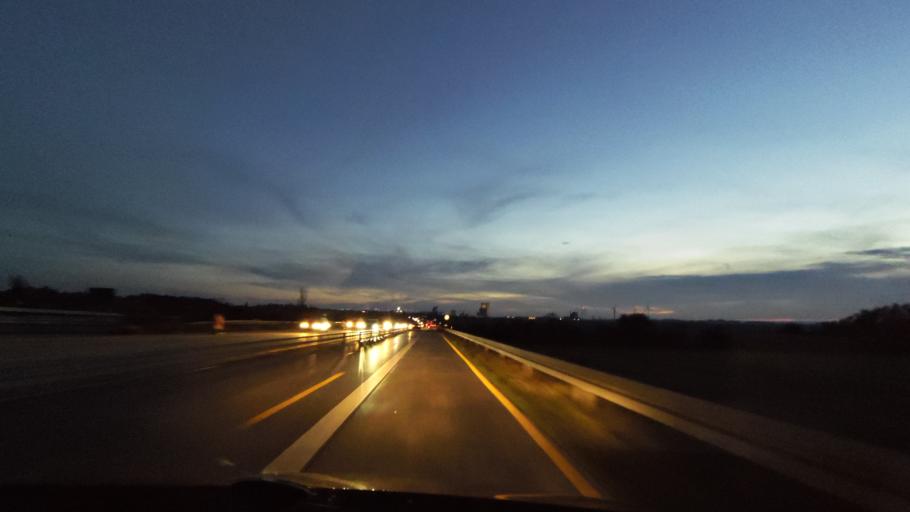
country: DE
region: Saxony-Anhalt
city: Osterfeld
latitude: 51.0570
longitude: 11.9476
